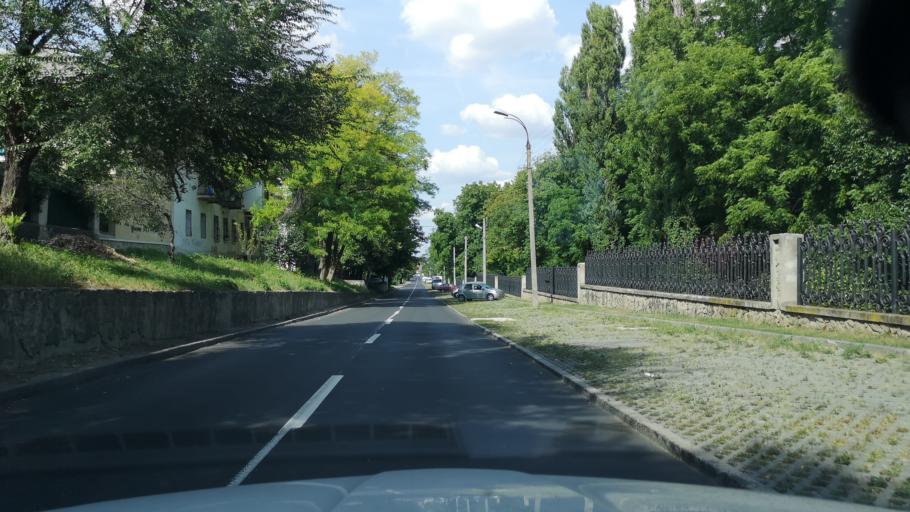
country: MD
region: Chisinau
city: Chisinau
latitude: 47.0236
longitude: 28.8092
